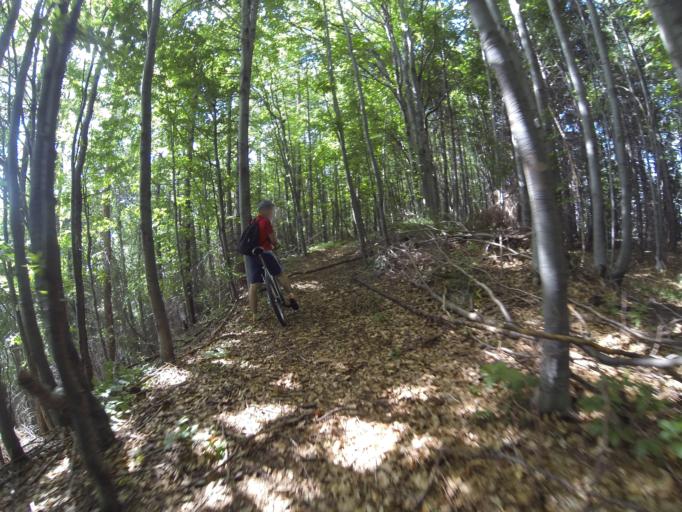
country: RO
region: Valcea
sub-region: Oras Baile Olanesti
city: Cheia
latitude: 45.2413
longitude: 24.1692
